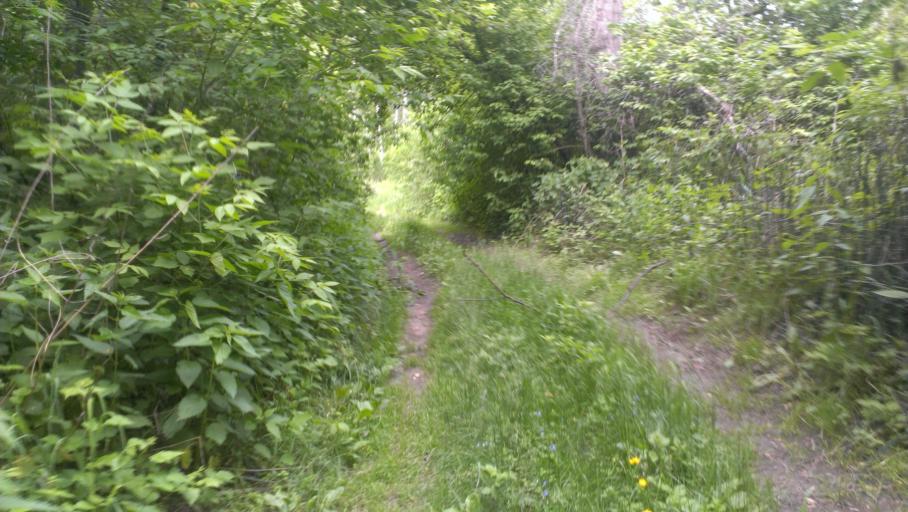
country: RU
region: Altai Krai
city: Sannikovo
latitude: 53.3424
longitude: 84.0593
